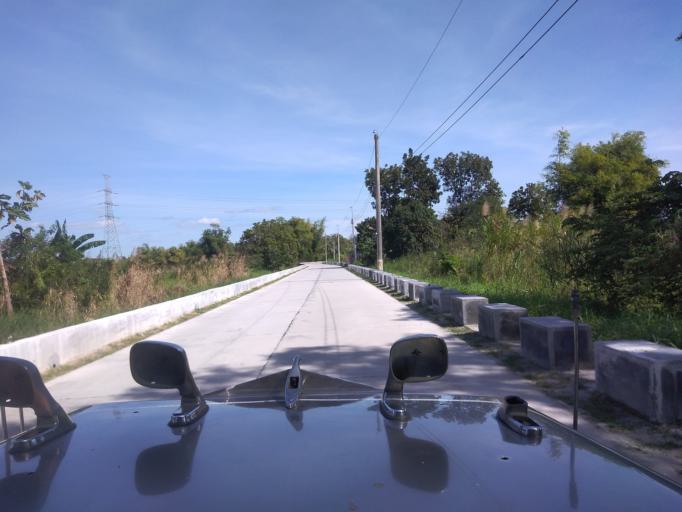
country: PH
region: Central Luzon
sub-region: Province of Pampanga
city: Magliman
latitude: 15.0260
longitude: 120.6649
